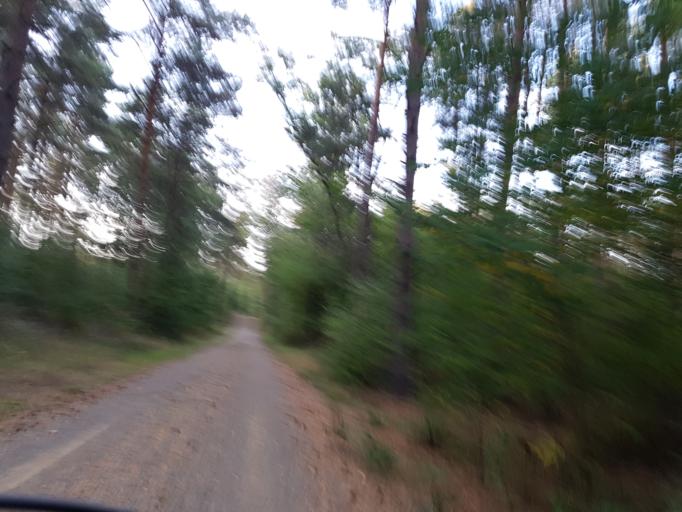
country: DE
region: Brandenburg
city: Trobitz
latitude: 51.5737
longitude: 13.4607
